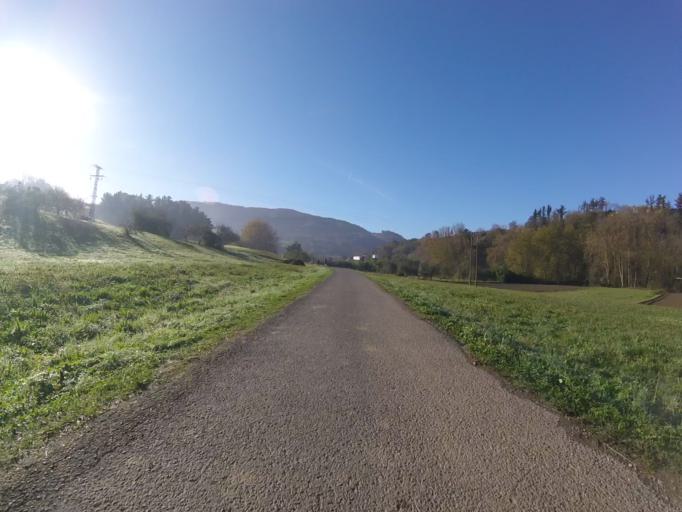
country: ES
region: Basque Country
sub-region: Provincia de Guipuzcoa
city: Usurbil
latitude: 43.2761
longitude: -2.0646
